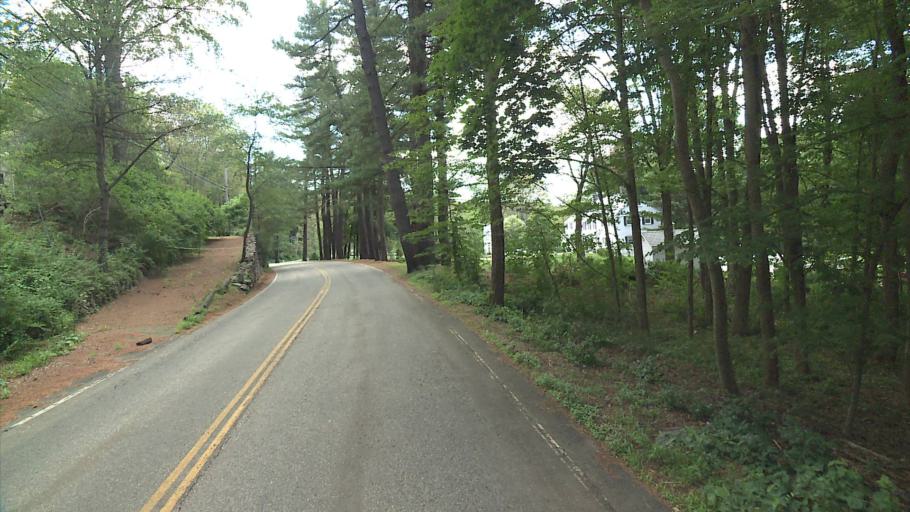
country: US
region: Connecticut
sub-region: Middlesex County
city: Higganum
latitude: 41.5459
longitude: -72.5462
